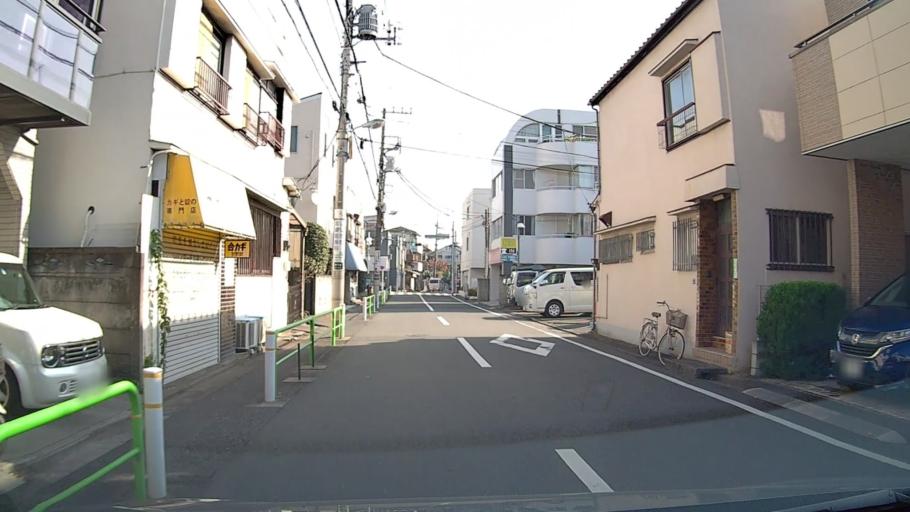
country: JP
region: Saitama
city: Kawaguchi
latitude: 35.7537
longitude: 139.6828
